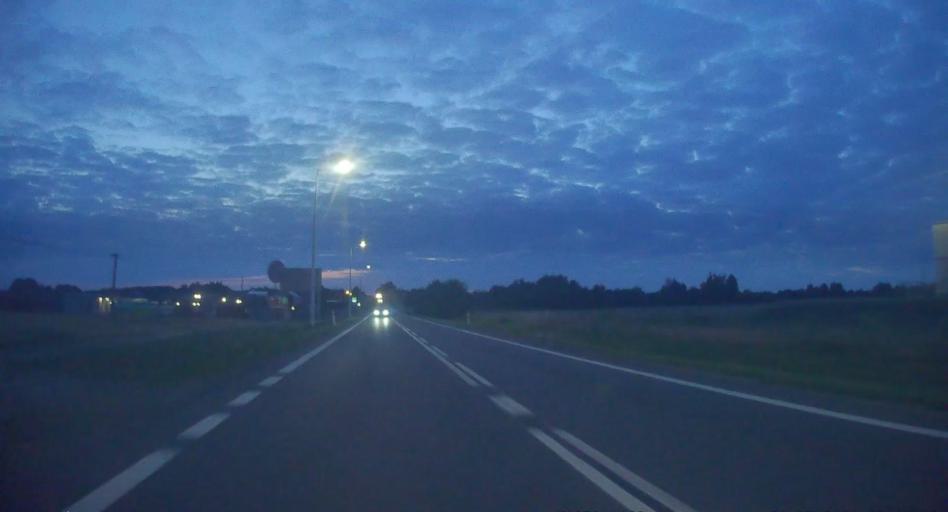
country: PL
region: Silesian Voivodeship
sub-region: Powiat klobucki
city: Kamyk
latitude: 50.8774
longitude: 18.9995
